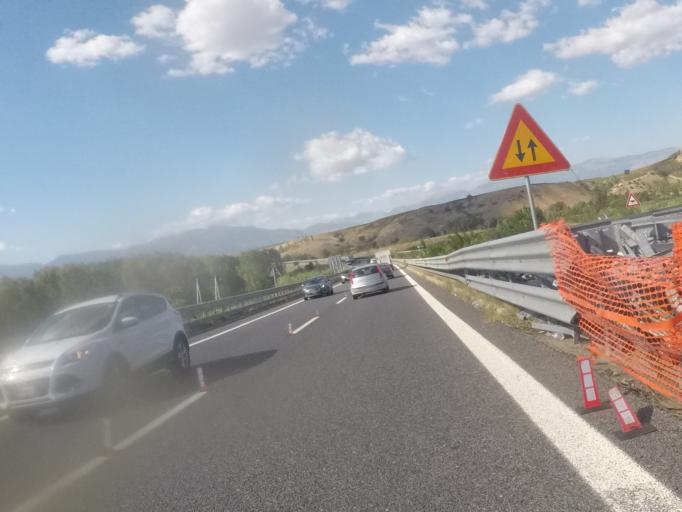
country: IT
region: Calabria
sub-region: Provincia di Cosenza
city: Tarsia
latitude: 39.6392
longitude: 16.2306
